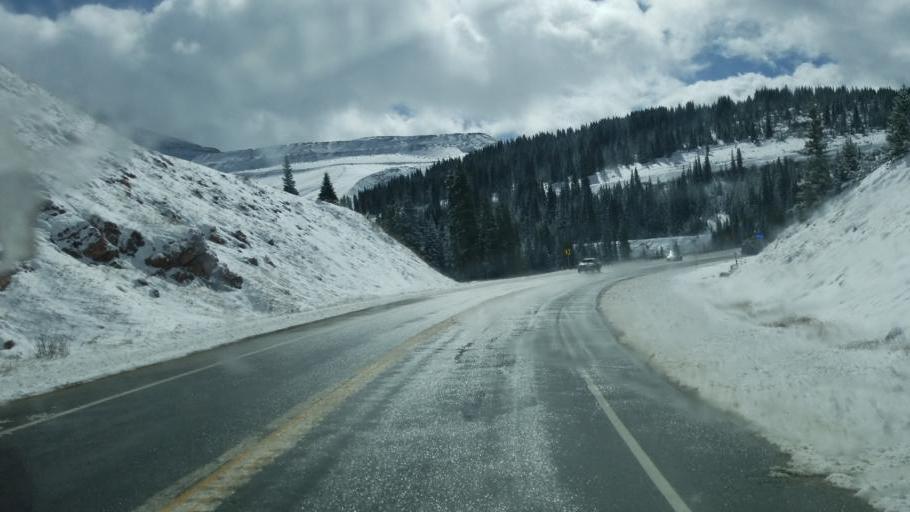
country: US
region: Colorado
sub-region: Summit County
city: Breckenridge
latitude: 39.3942
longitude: -106.1868
